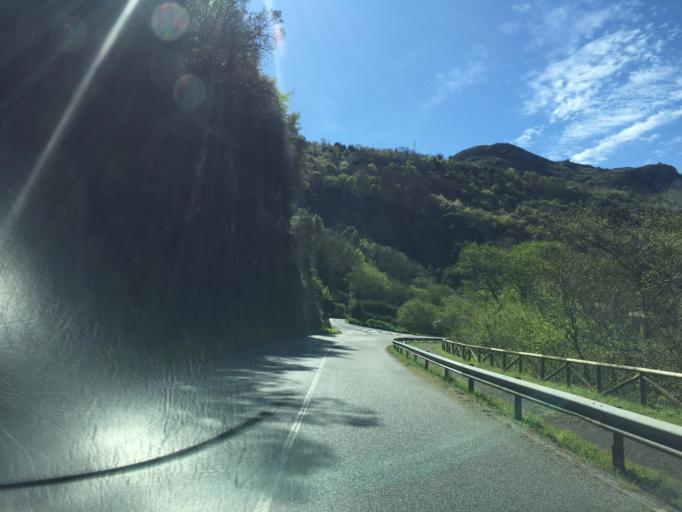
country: ES
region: Asturias
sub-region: Province of Asturias
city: Proaza
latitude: 43.2935
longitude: -5.9823
